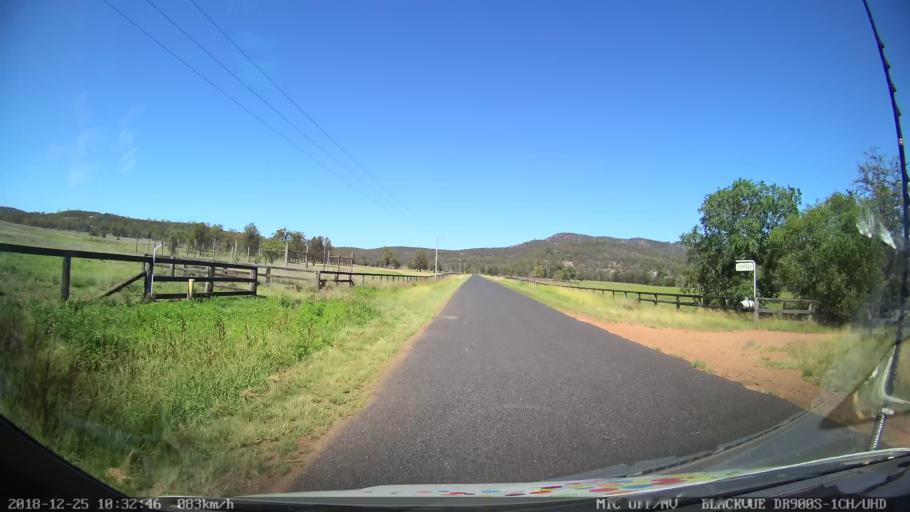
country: AU
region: New South Wales
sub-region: Upper Hunter Shire
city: Merriwa
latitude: -32.3777
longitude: 150.4143
